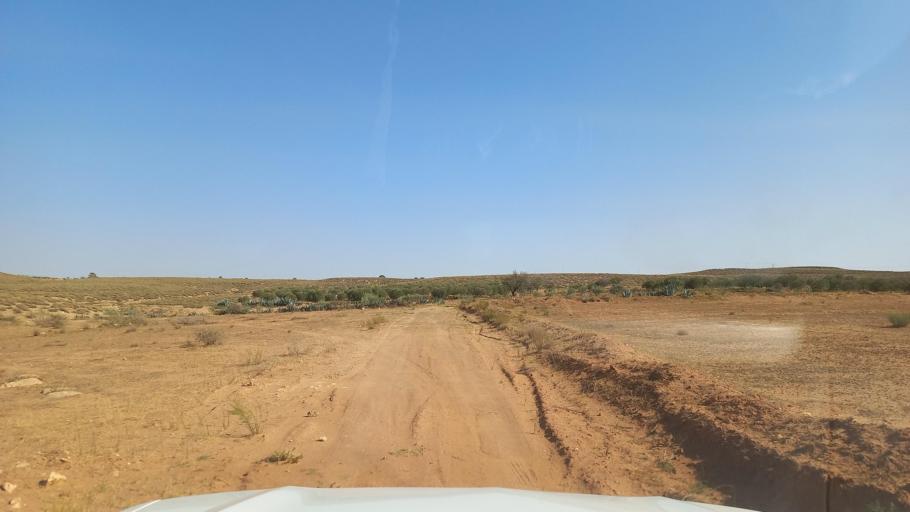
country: TN
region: Al Qasrayn
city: Kasserine
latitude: 35.2037
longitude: 8.9730
